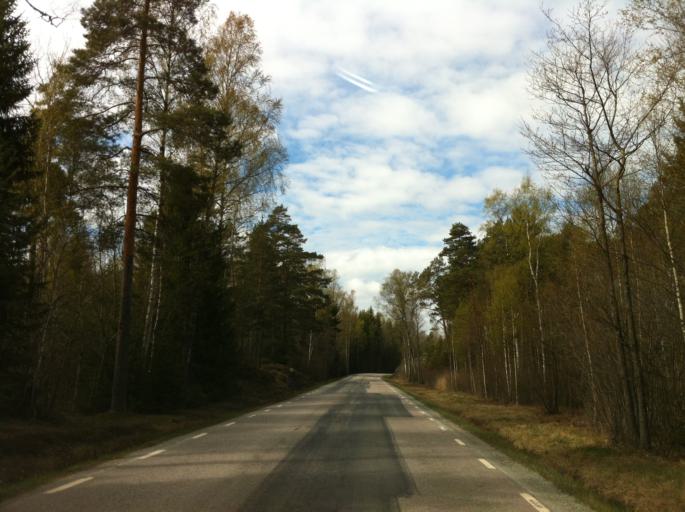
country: SE
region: OEstergoetland
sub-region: Valdemarsviks Kommun
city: Valdemarsvik
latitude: 58.1864
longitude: 16.7902
